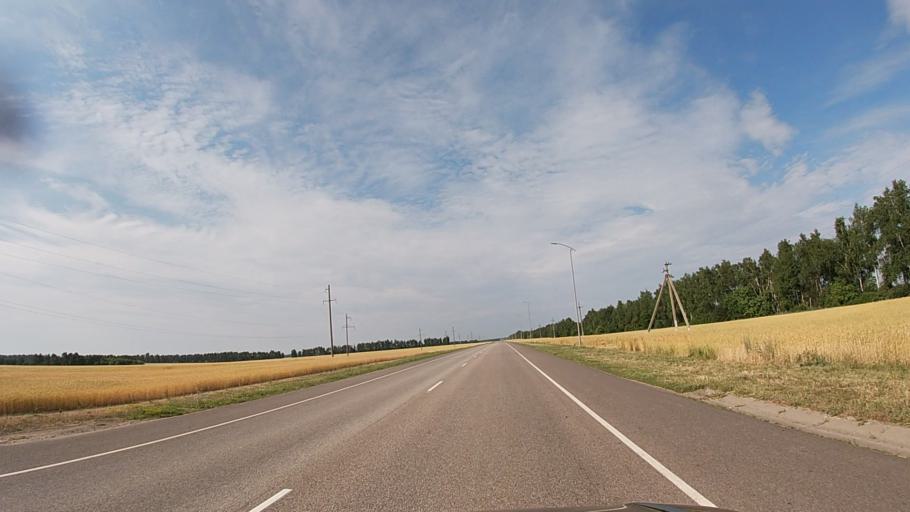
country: RU
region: Belgorod
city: Proletarskiy
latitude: 50.8278
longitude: 35.7618
